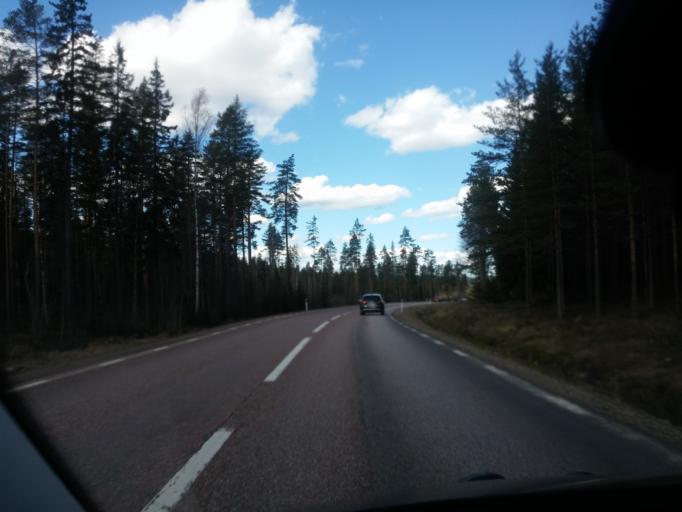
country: SE
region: Dalarna
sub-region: Faluns Kommun
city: Svardsjo
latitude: 60.7755
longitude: 15.7538
